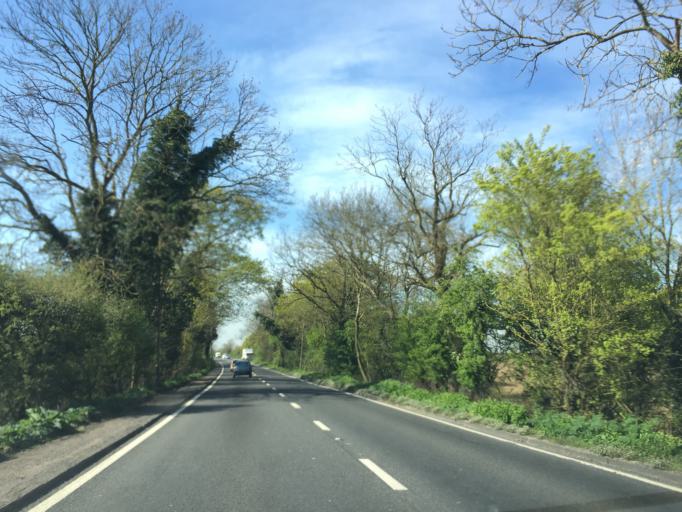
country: GB
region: England
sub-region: Essex
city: Epping
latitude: 51.7344
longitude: 0.1264
